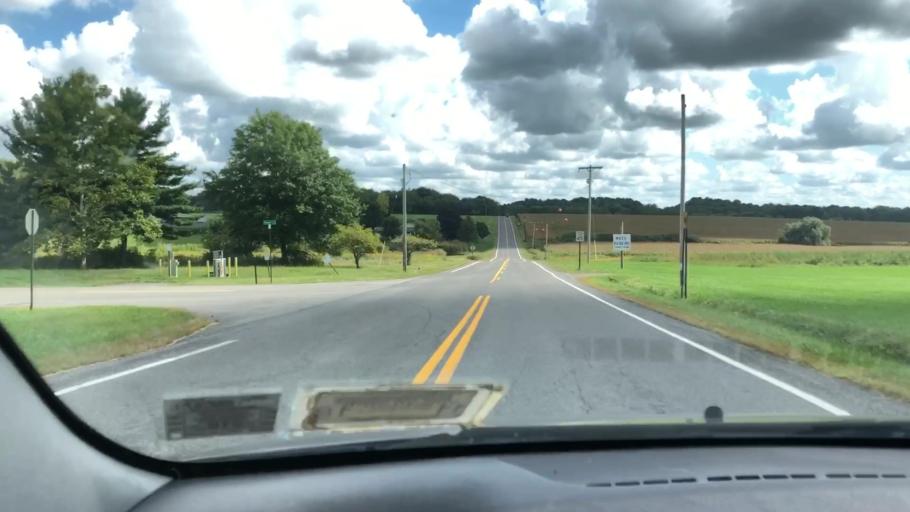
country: US
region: New York
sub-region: Wayne County
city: Macedon
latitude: 43.1164
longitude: -77.3133
